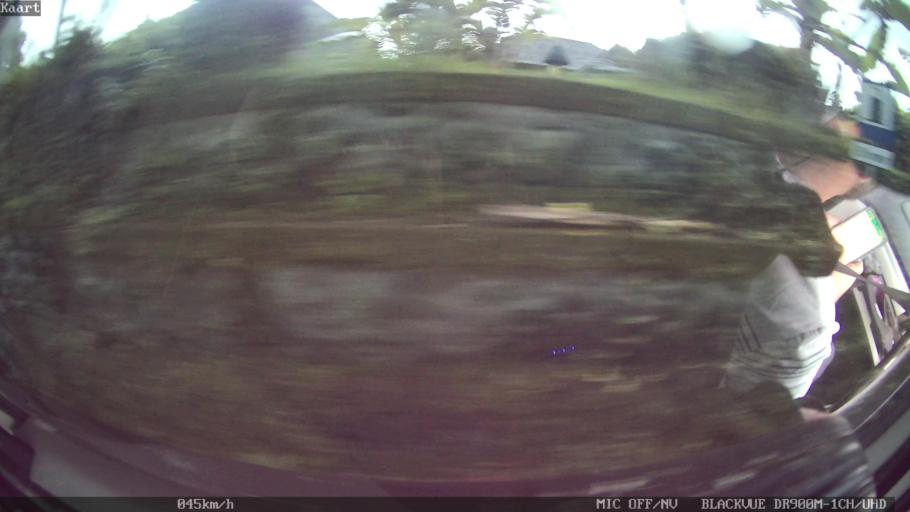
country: ID
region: Bali
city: Banjar Sayanbaleran
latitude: -8.5036
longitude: 115.1873
